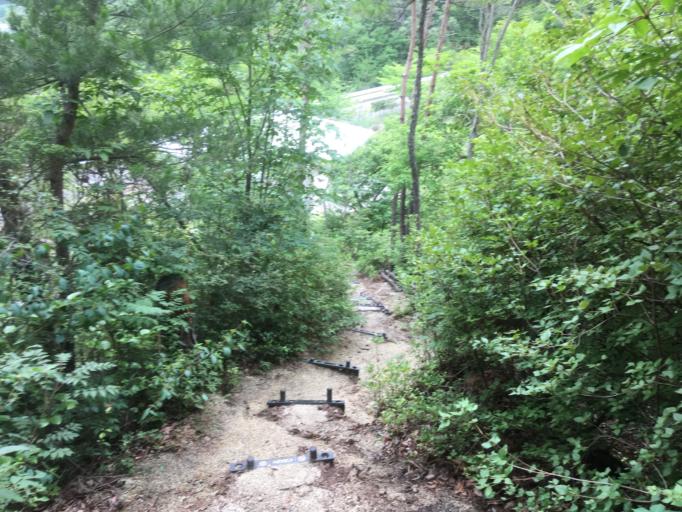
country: JP
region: Nara
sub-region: Ikoma-shi
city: Ikoma
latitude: 34.7381
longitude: 135.6878
